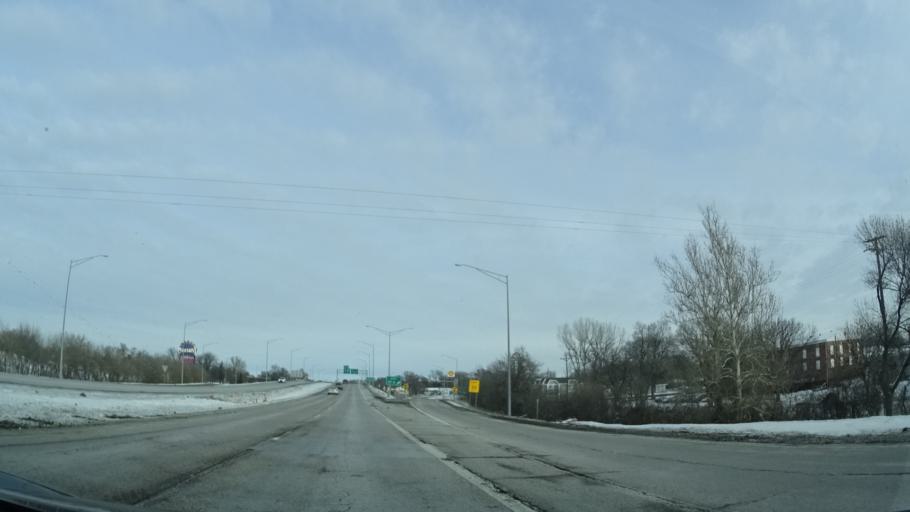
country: US
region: Nebraska
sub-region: Douglas County
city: Omaha
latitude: 41.2509
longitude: -95.9067
